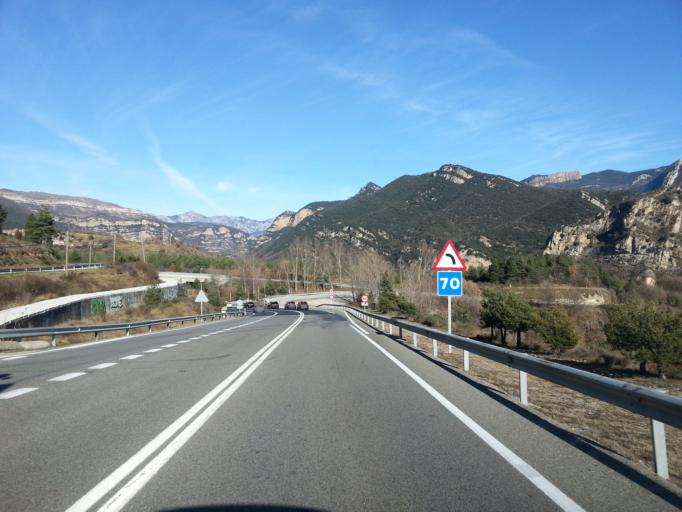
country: ES
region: Catalonia
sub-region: Provincia de Barcelona
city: Berga
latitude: 42.1403
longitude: 1.8657
